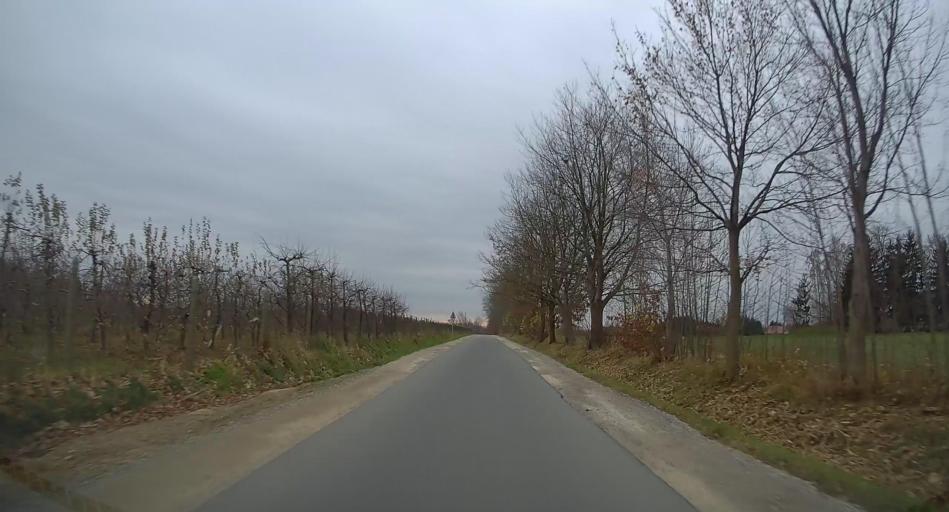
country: PL
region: Lodz Voivodeship
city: Zabia Wola
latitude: 52.0073
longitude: 20.6563
